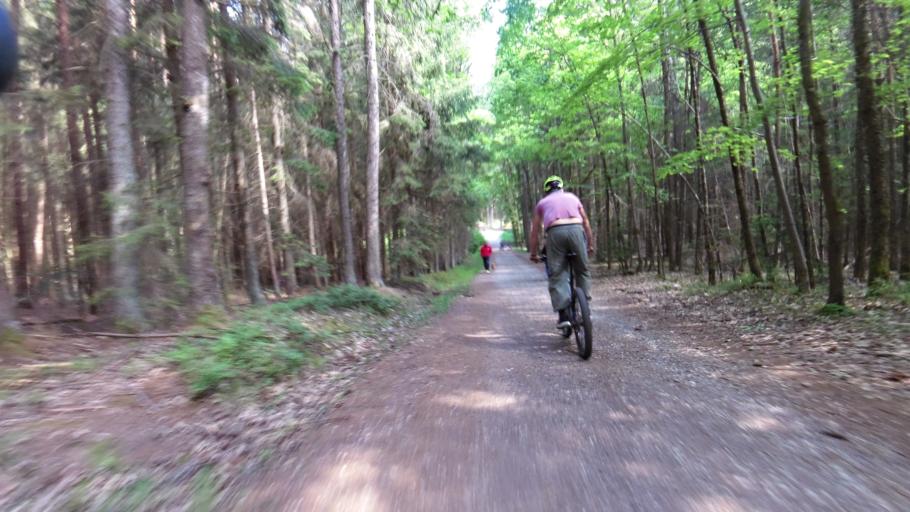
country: DE
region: Bavaria
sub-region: Regierungsbezirk Mittelfranken
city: Pleinfeld
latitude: 49.1142
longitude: 10.9618
